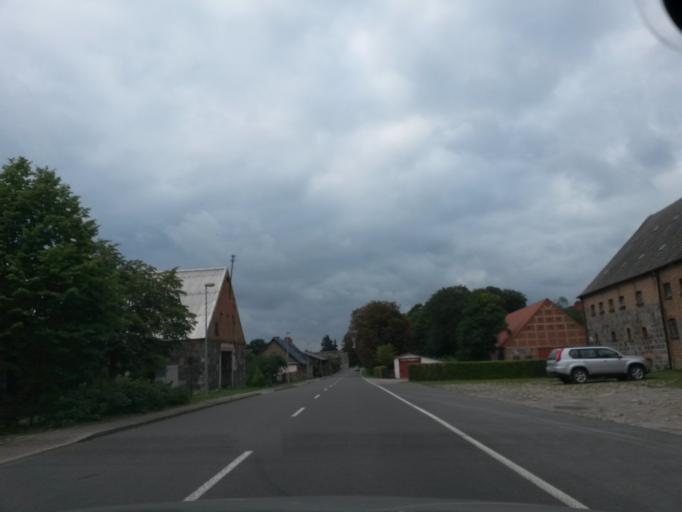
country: DE
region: Brandenburg
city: Angermunde
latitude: 53.1100
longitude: 13.9096
